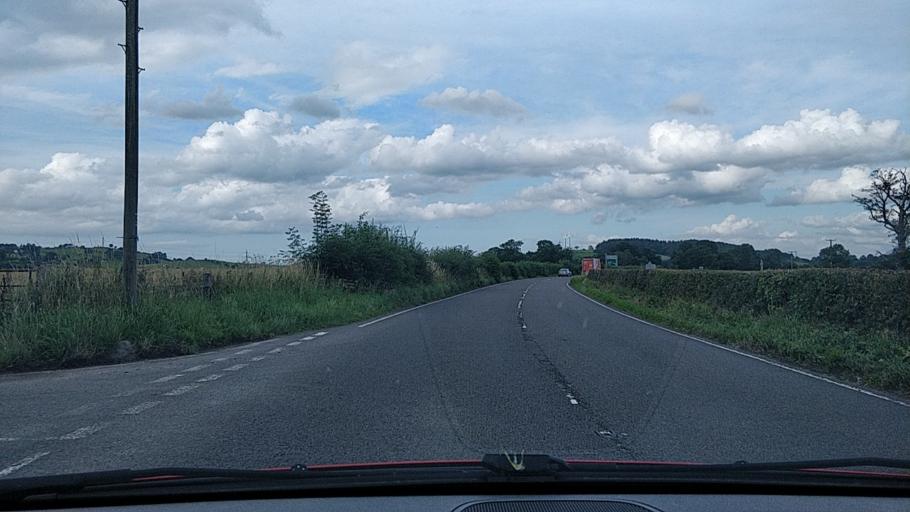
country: GB
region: Wales
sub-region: Denbighshire
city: Corwen
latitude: 52.9883
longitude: -3.3904
